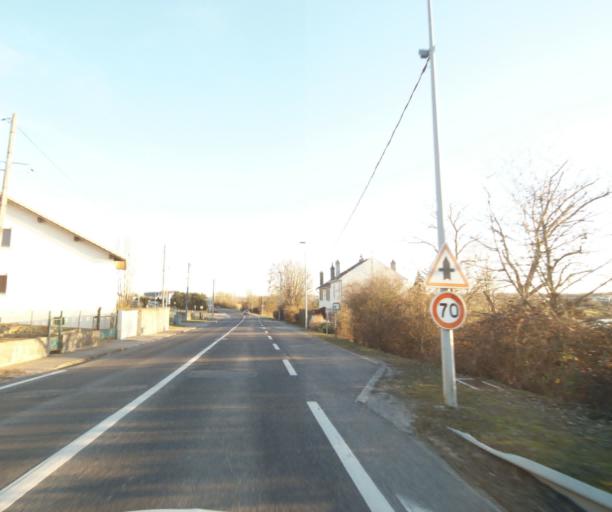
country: FR
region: Lorraine
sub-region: Departement de Meurthe-et-Moselle
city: Laneuveville-devant-Nancy
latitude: 48.6685
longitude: 6.2330
